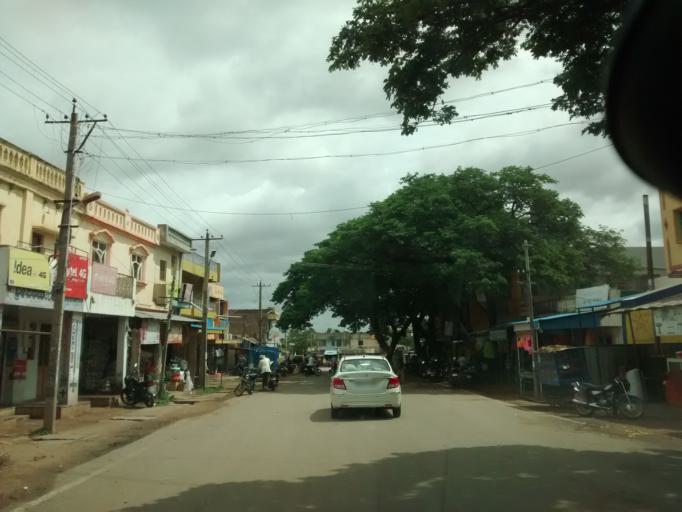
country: IN
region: Karnataka
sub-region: Tumkur
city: Kodigenahalli
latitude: 13.7206
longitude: 77.3871
